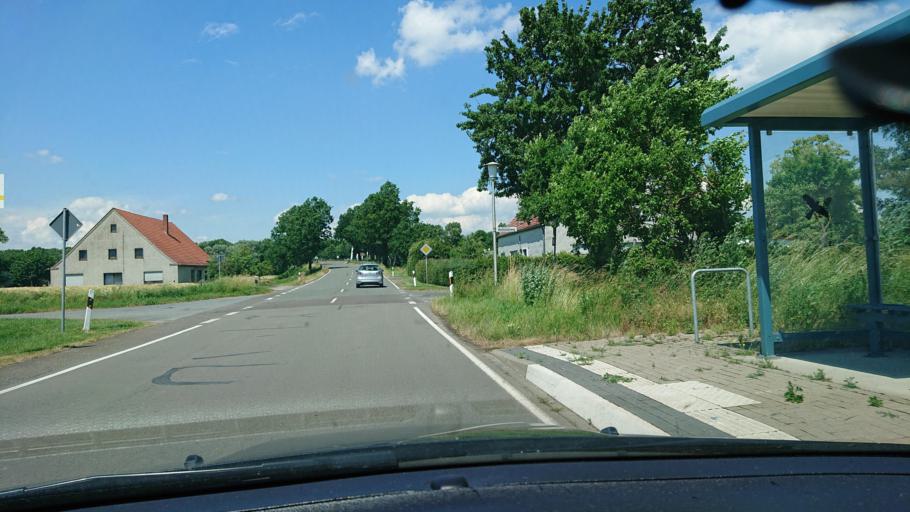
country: DE
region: North Rhine-Westphalia
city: Preussisch Oldendorf
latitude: 52.3384
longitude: 8.4611
